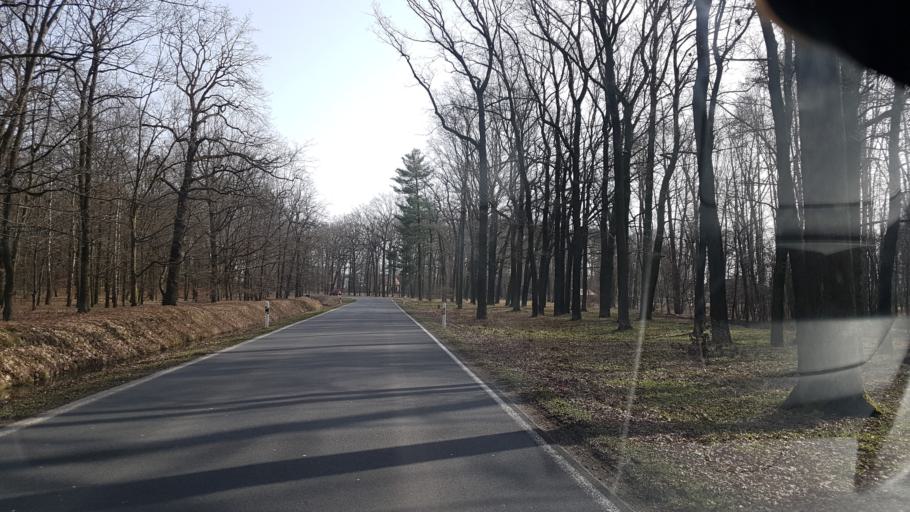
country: DE
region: Brandenburg
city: Cottbus
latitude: 51.7390
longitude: 14.3590
